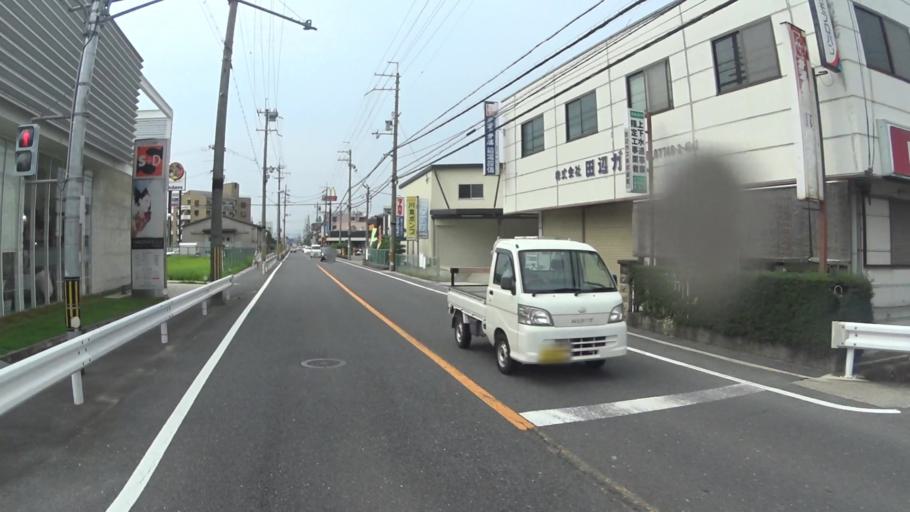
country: JP
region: Kyoto
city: Tanabe
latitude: 34.7850
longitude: 135.7870
